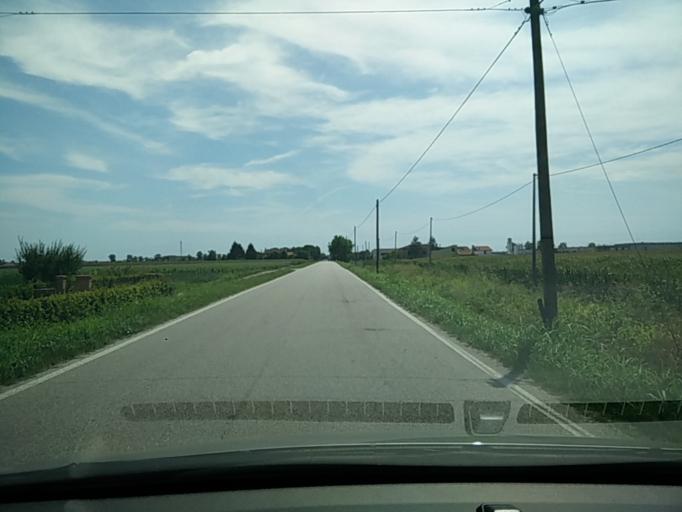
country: IT
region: Veneto
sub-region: Provincia di Venezia
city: Iesolo
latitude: 45.5559
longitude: 12.6518
